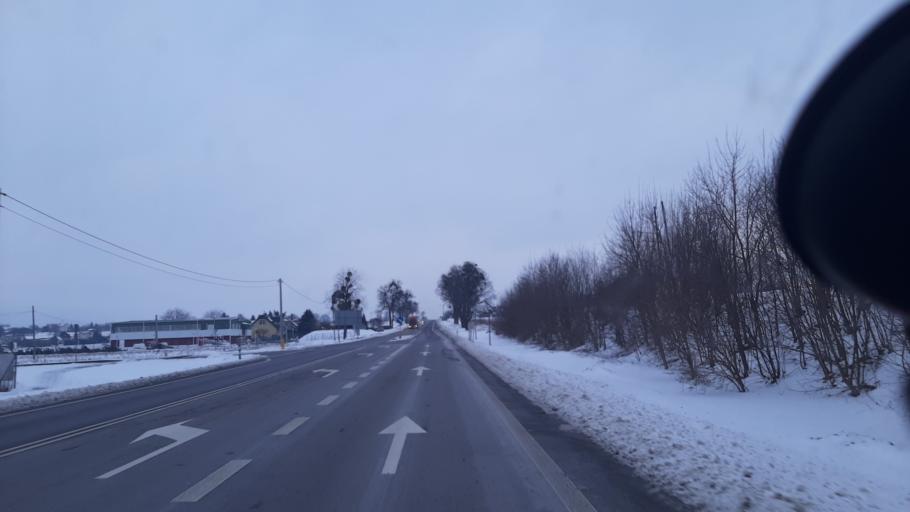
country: PL
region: Lublin Voivodeship
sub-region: Powiat pulawski
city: Markuszow
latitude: 51.3711
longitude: 22.2747
